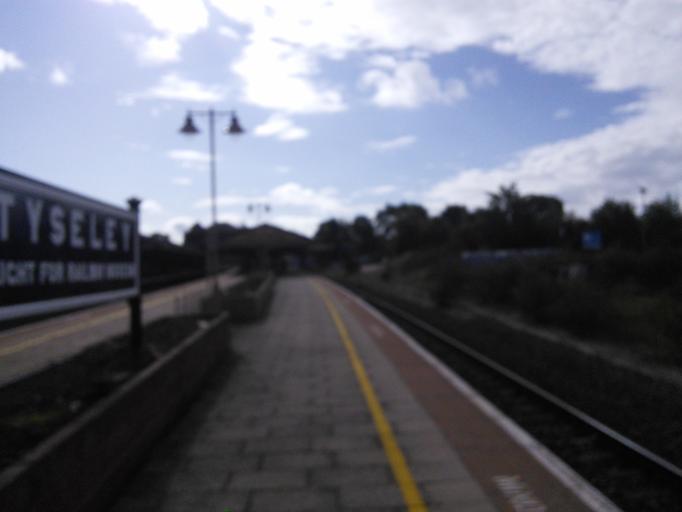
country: GB
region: England
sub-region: City and Borough of Birmingham
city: Acocks Green
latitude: 52.4546
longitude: -1.8405
